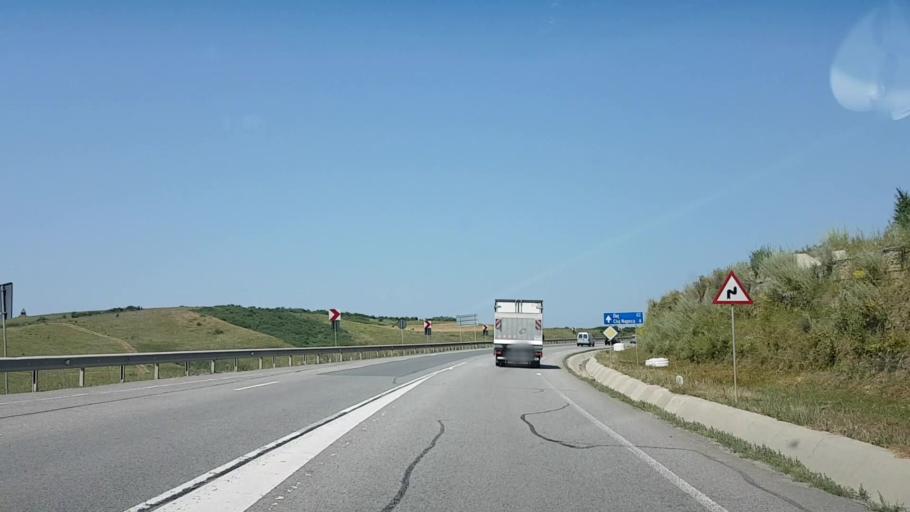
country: RO
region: Cluj
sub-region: Comuna Apahida
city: Dezmir
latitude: 46.7685
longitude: 23.6907
